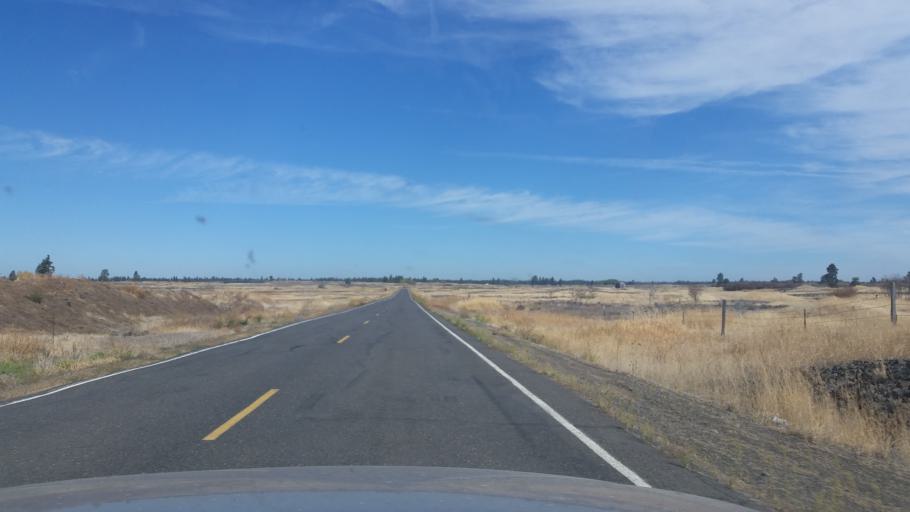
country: US
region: Washington
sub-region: Spokane County
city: Medical Lake
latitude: 47.3861
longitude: -117.8422
